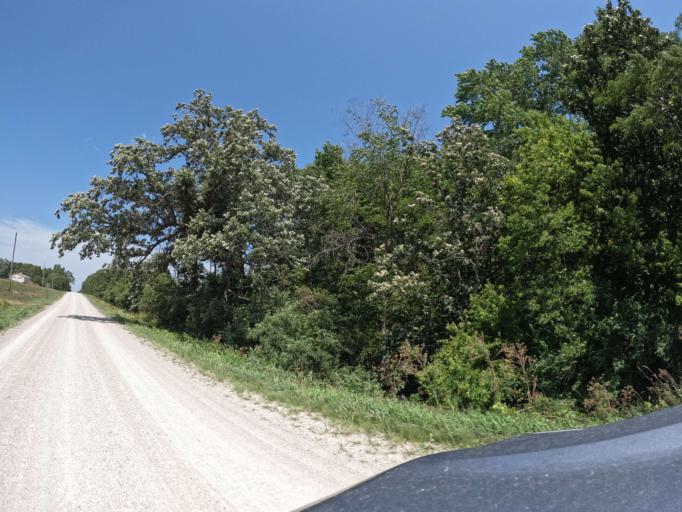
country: US
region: Iowa
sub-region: Henry County
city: Mount Pleasant
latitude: 40.9460
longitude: -91.6509
